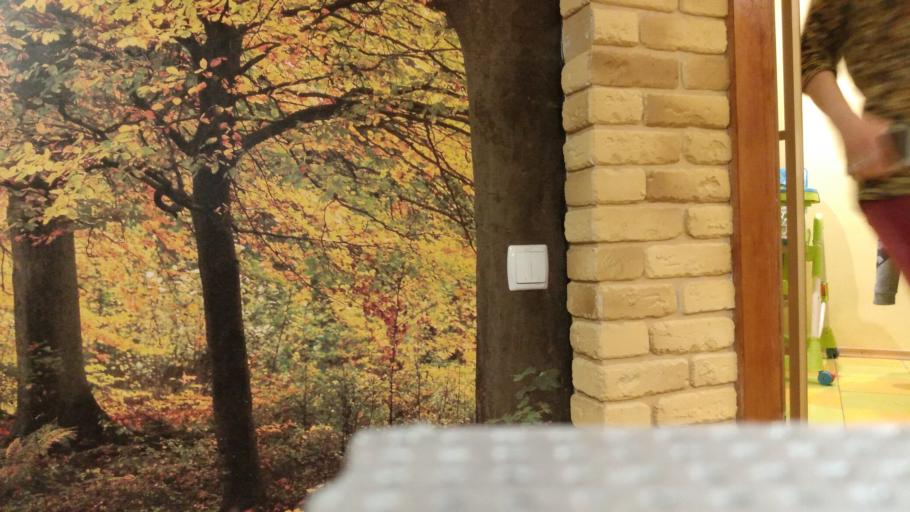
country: RU
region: Vologda
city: Babayevo
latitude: 59.3700
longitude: 35.9954
